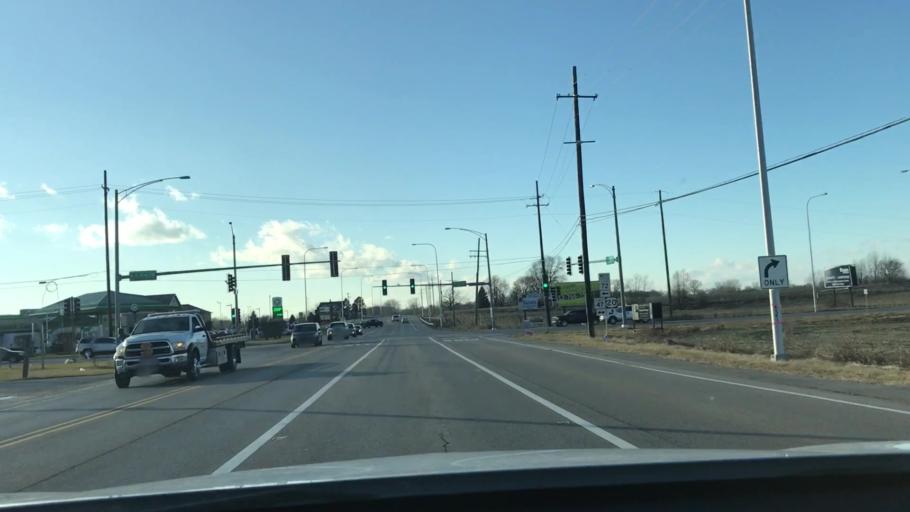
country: US
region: Illinois
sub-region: Kane County
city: Pingree Grove
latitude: 42.0886
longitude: -88.4559
